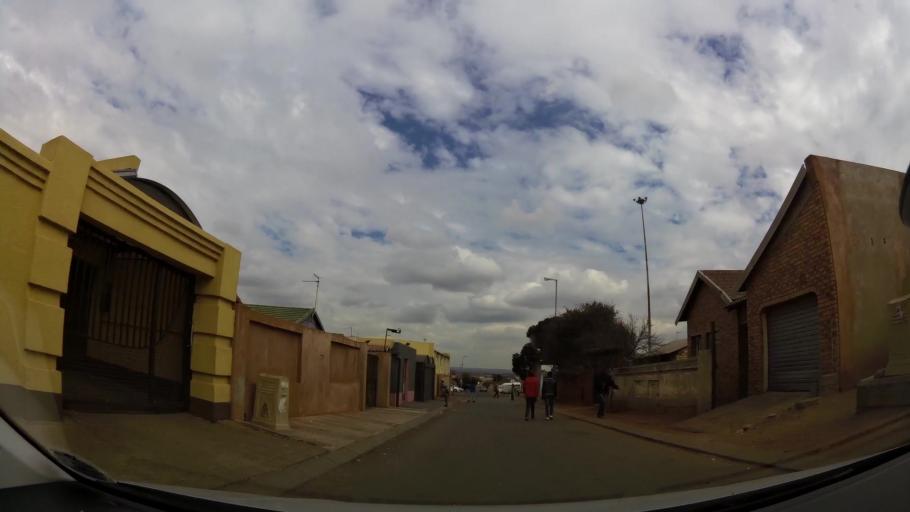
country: ZA
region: Gauteng
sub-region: City of Johannesburg Metropolitan Municipality
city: Soweto
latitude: -26.2818
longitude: 27.8533
